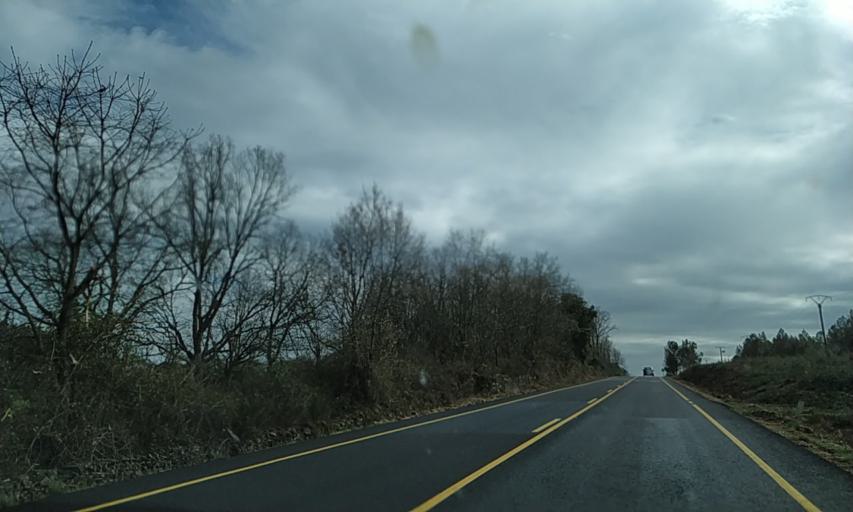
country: ES
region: Castille and Leon
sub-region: Provincia de Salamanca
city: Robleda
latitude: 40.3689
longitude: -6.6189
